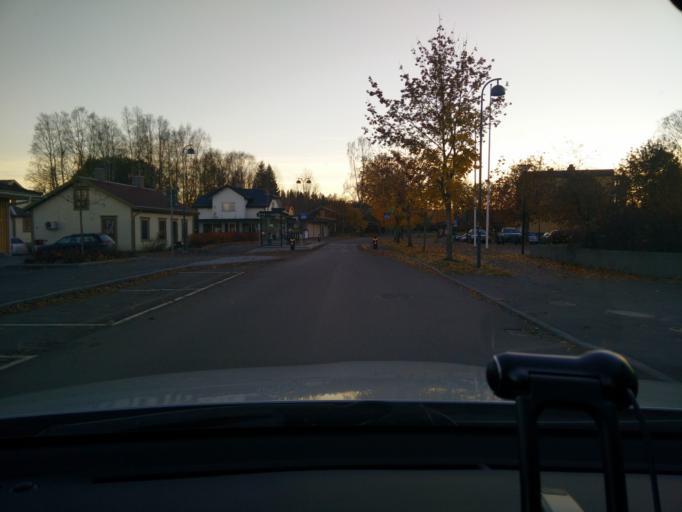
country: SE
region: Vaesternorrland
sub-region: Sundsvalls Kommun
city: Matfors
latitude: 62.3466
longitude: 17.0202
